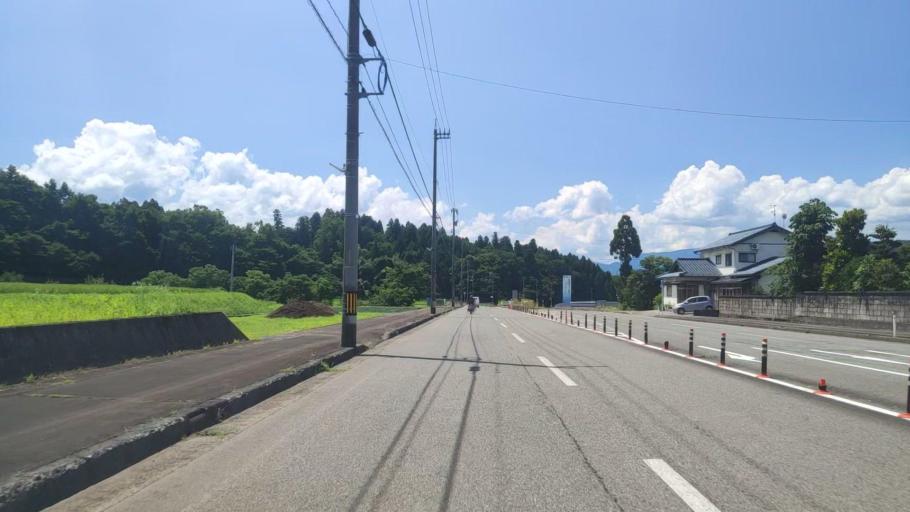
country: JP
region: Fukui
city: Katsuyama
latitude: 36.0333
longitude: 136.5202
